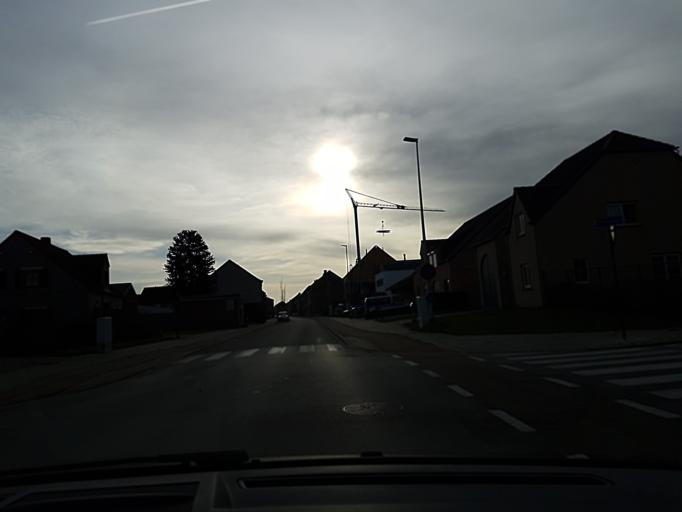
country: BE
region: Flanders
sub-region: Provincie Vlaams-Brabant
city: Herent
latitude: 50.9321
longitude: 4.6893
